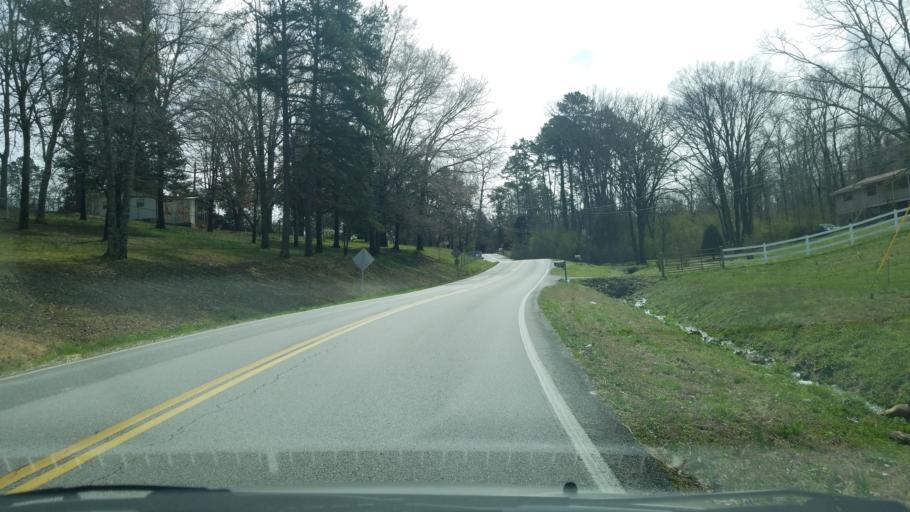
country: US
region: Tennessee
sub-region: Hamilton County
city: Harrison
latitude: 35.1413
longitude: -85.0907
